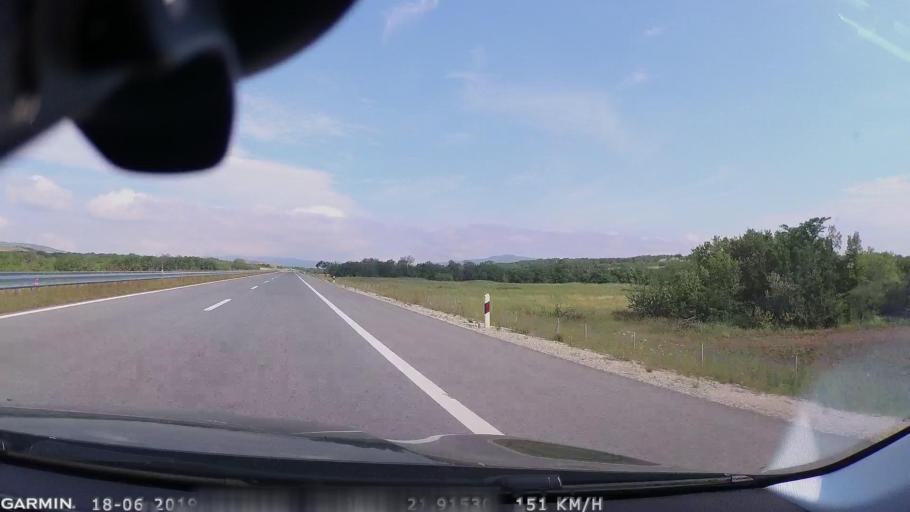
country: MK
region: Sveti Nikole
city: Gorobinci
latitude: 41.9023
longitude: 21.9137
